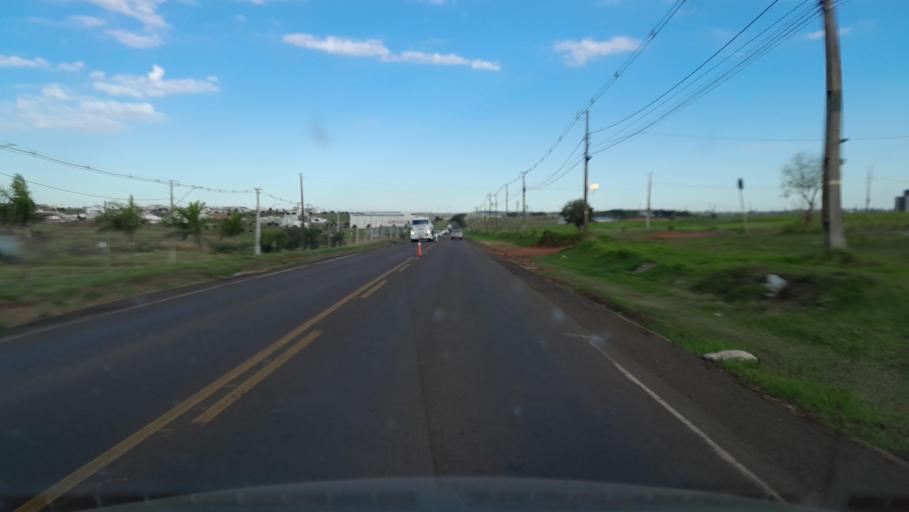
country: BR
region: Parana
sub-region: Umuarama
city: Umuarama
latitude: -23.7544
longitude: -53.2721
